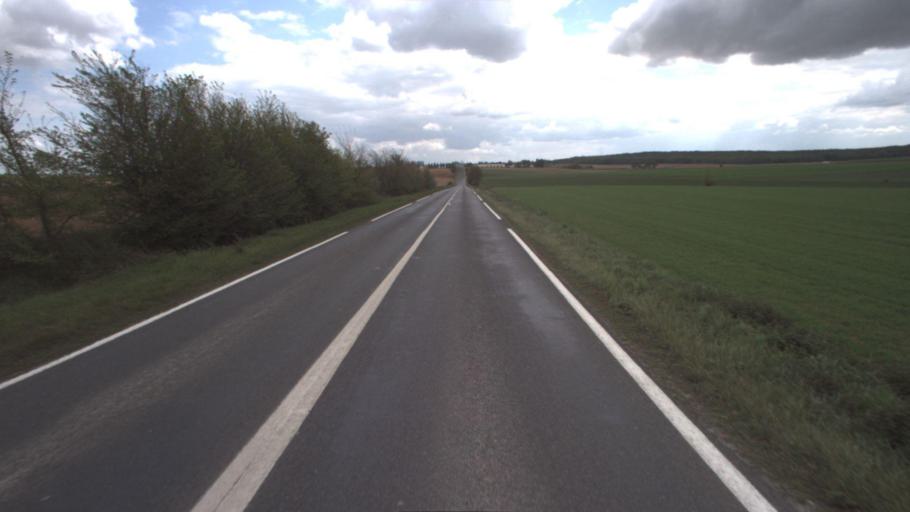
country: FR
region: Ile-de-France
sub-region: Departement de Seine-et-Marne
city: Saint-Soupplets
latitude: 49.0506
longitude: 2.7882
